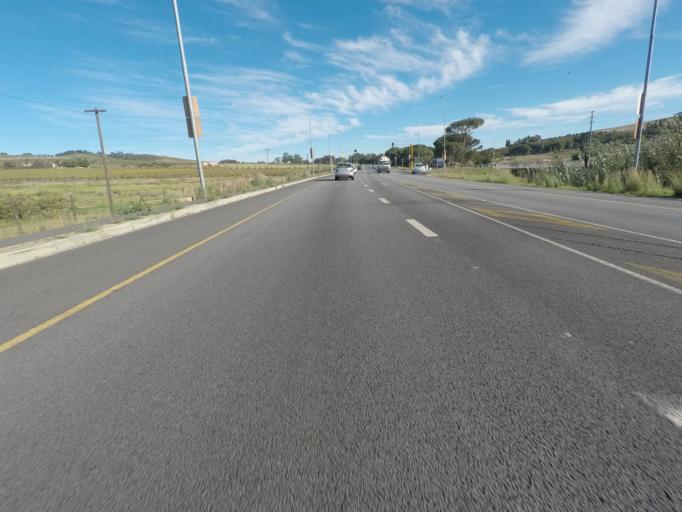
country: ZA
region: Western Cape
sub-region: Cape Winelands District Municipality
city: Stellenbosch
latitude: -33.9028
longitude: 18.8407
